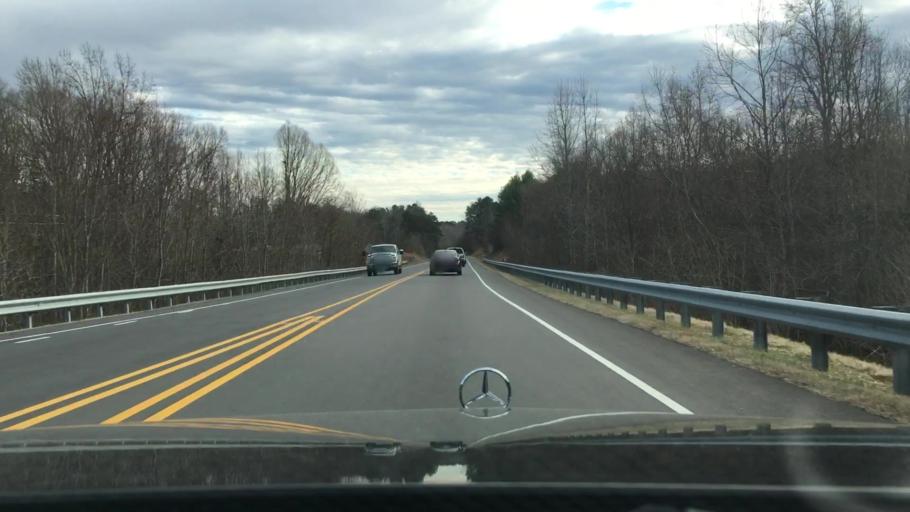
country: US
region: North Carolina
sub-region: Caswell County
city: Yanceyville
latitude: 36.4295
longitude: -79.3584
